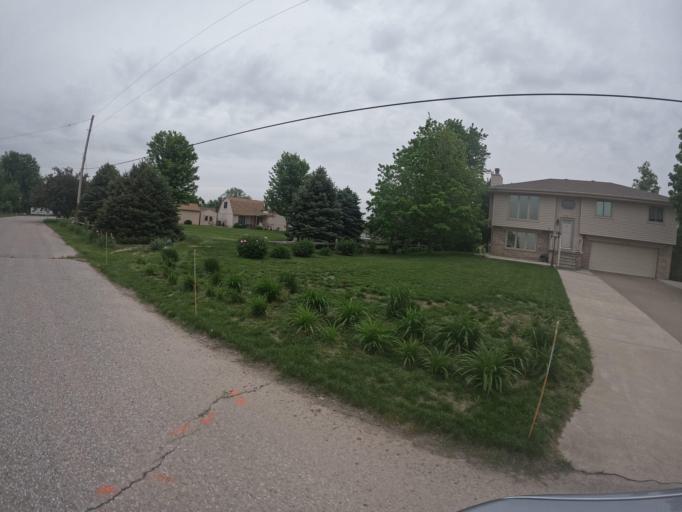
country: US
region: Nebraska
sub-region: Sarpy County
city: Offutt Air Force Base
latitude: 41.0562
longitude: -95.9576
